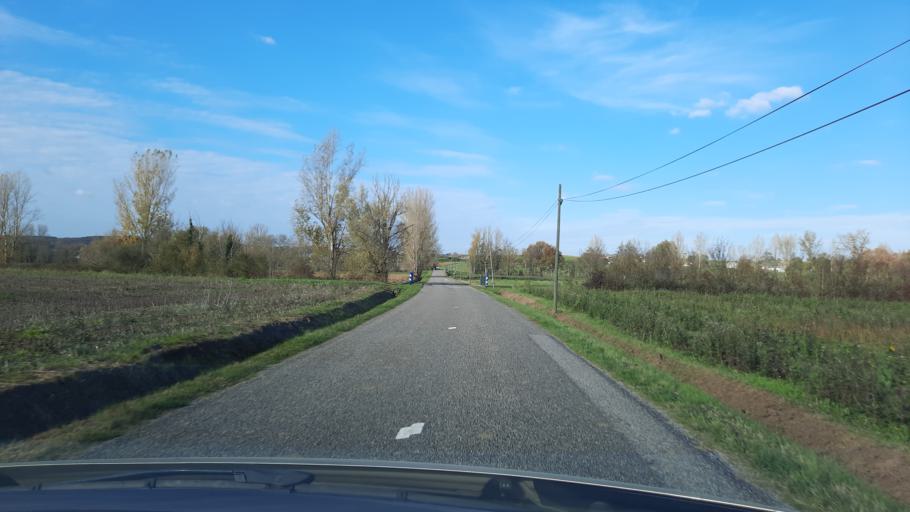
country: FR
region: Midi-Pyrenees
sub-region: Departement du Tarn-et-Garonne
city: Lafrancaise
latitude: 44.1587
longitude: 1.2657
